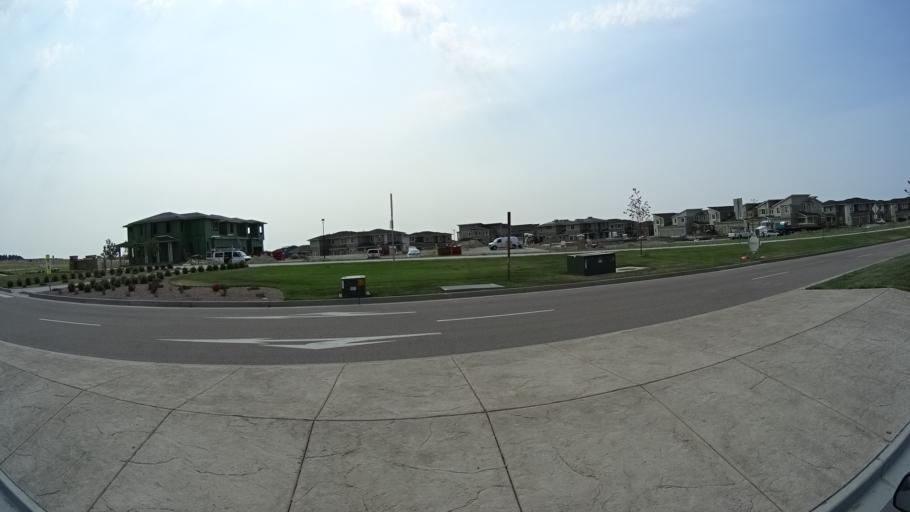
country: US
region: Colorado
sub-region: El Paso County
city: Black Forest
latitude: 38.9732
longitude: -104.7163
